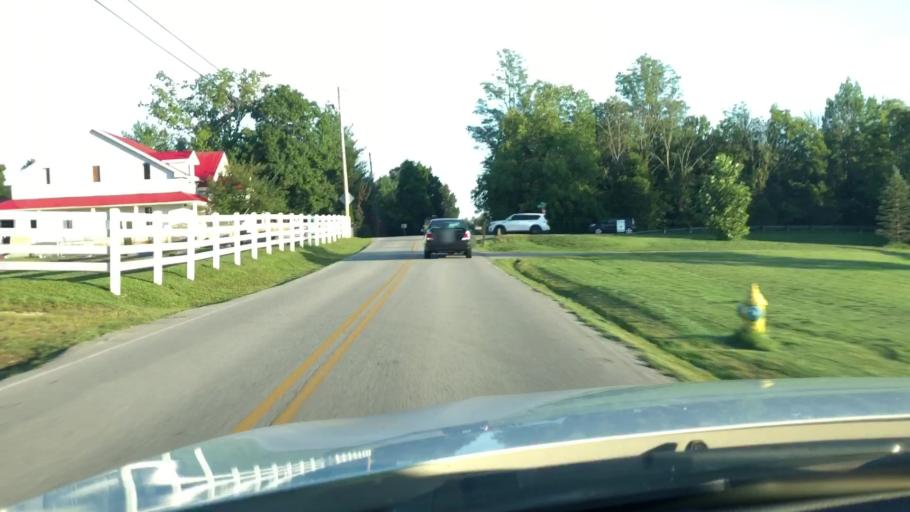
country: US
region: Kentucky
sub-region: Jefferson County
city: Middletown
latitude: 38.2110
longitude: -85.5042
